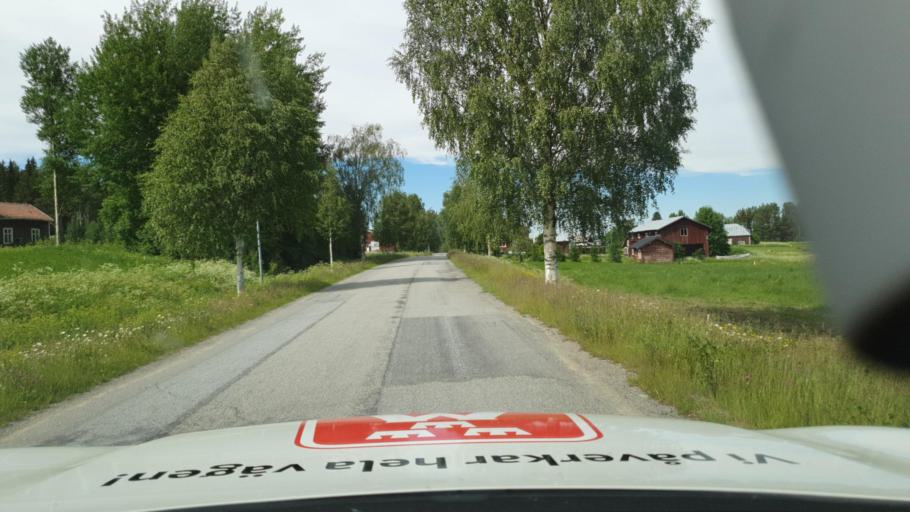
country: SE
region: Vaesterbotten
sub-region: Skelleftea Kommun
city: Burtraesk
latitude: 64.4261
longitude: 20.5312
